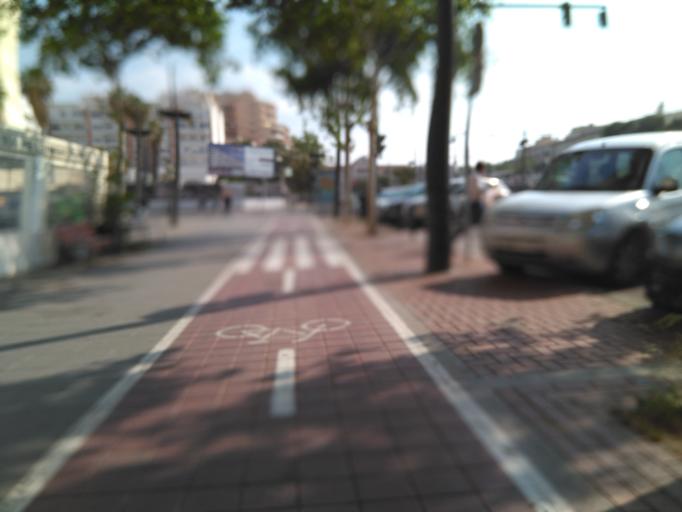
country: ES
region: Valencia
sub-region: Provincia de Valencia
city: Valencia
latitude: 39.4829
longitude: -0.3720
